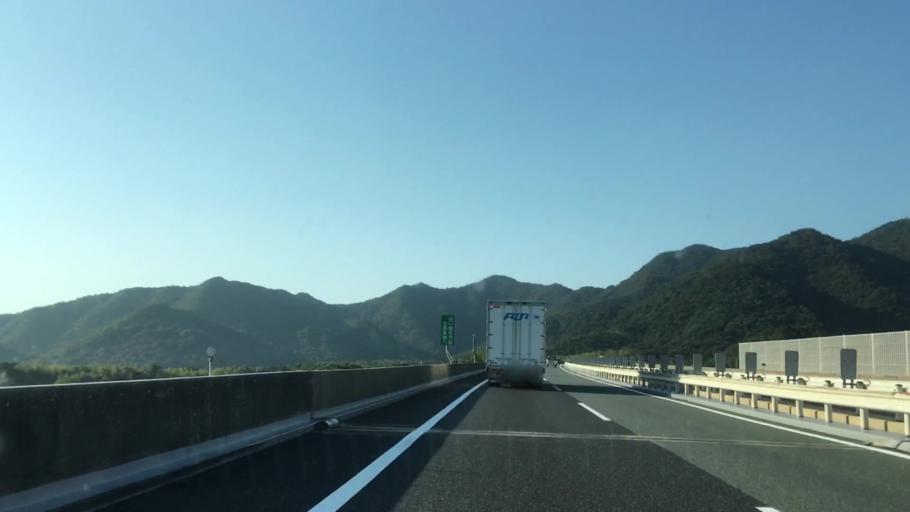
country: JP
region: Yamaguchi
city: Ogori-shimogo
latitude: 34.0934
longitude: 131.4557
